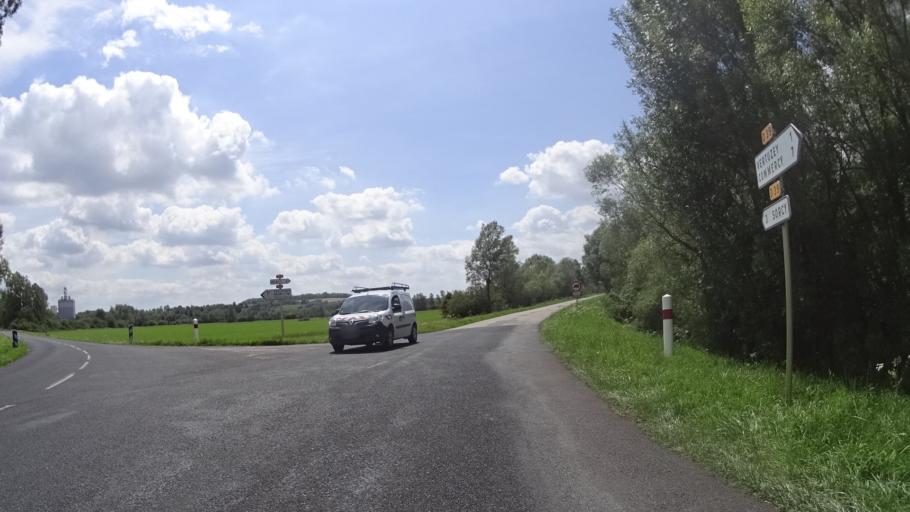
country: FR
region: Lorraine
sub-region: Departement de la Meuse
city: Euville
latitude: 48.7288
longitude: 5.6635
